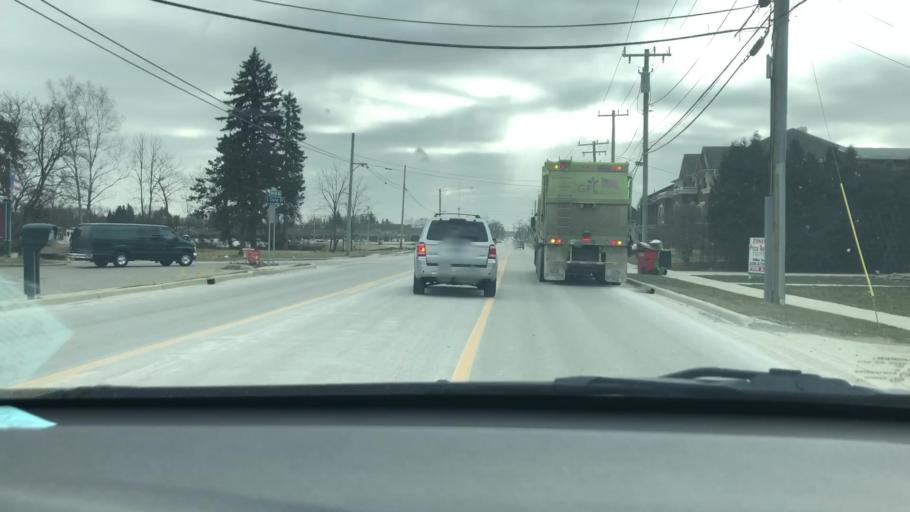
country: US
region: Michigan
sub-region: Macomb County
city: Shelby
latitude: 42.7309
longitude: -83.0362
